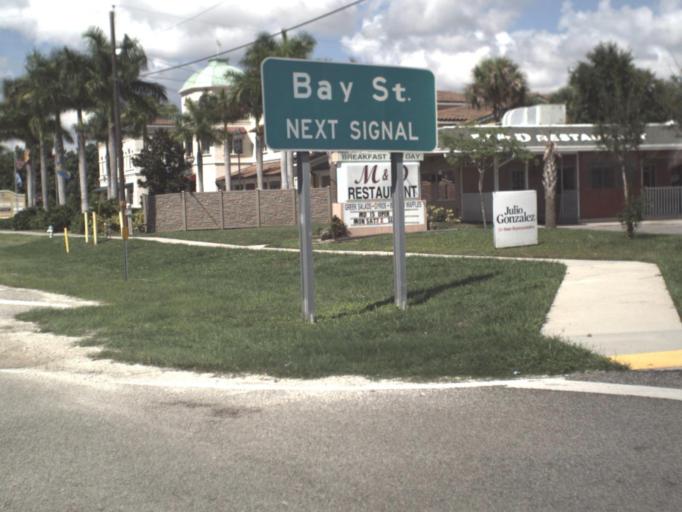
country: US
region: Florida
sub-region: Sarasota County
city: Osprey
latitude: 27.1944
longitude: -82.4896
